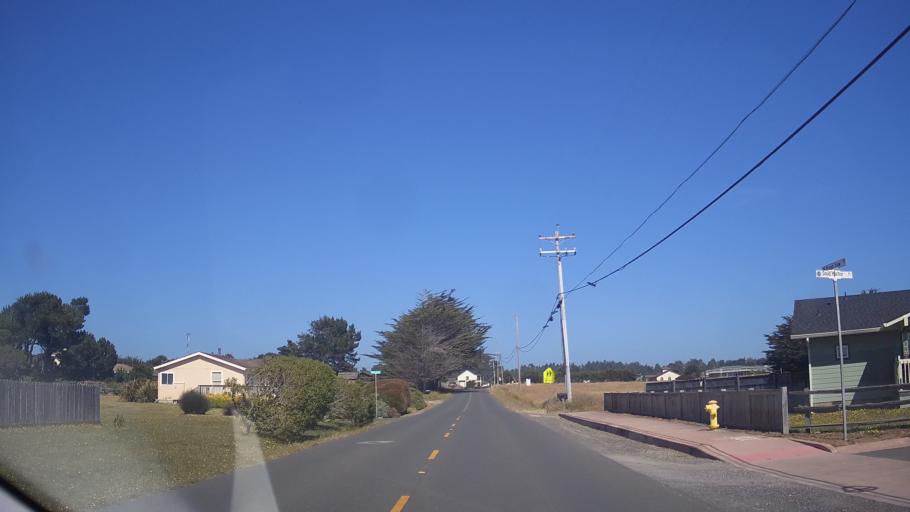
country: US
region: California
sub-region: Mendocino County
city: Fort Bragg
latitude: 39.4233
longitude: -123.8126
